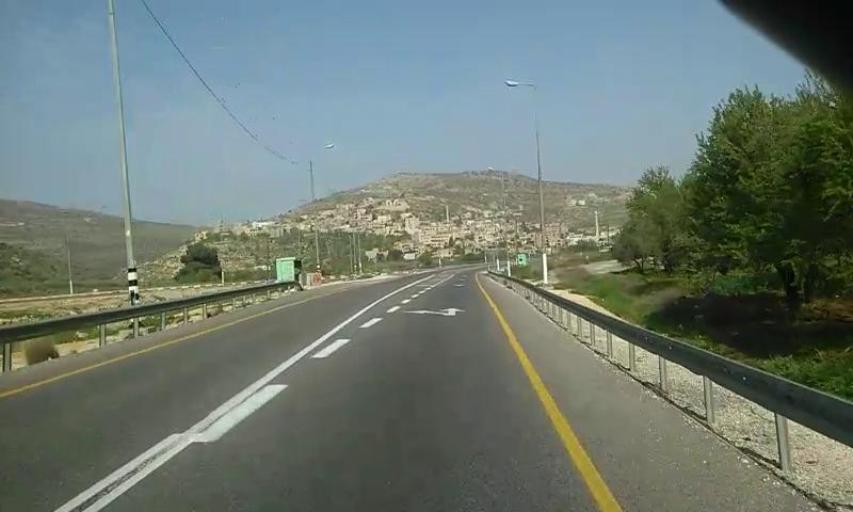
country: PS
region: West Bank
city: Al Lubban ash Sharqiyah
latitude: 32.0691
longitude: 35.2473
